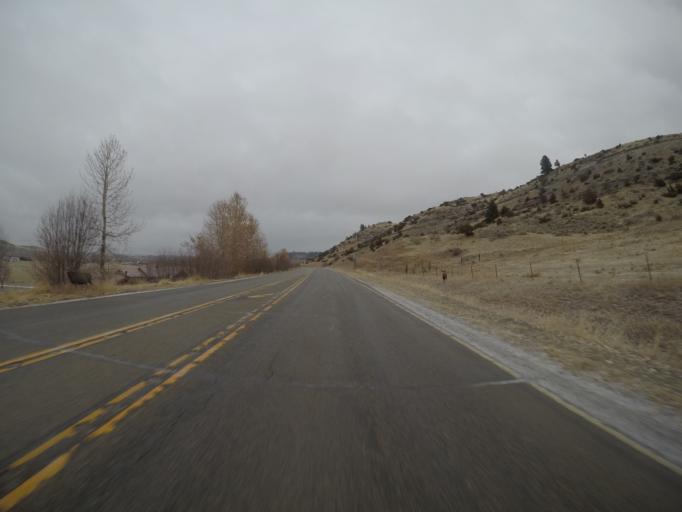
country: US
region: Montana
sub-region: Stillwater County
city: Absarokee
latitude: 45.5223
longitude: -109.4549
